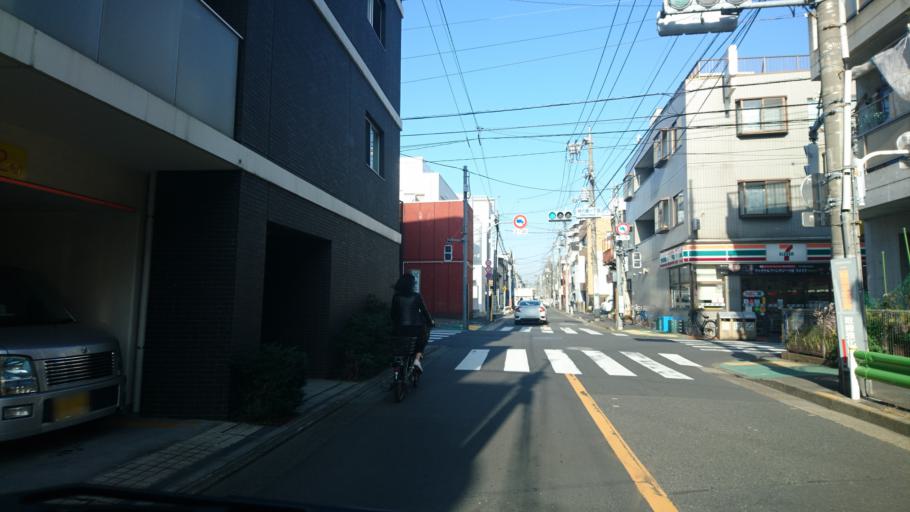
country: JP
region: Kanagawa
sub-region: Kawasaki-shi
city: Kawasaki
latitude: 35.5535
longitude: 139.7158
